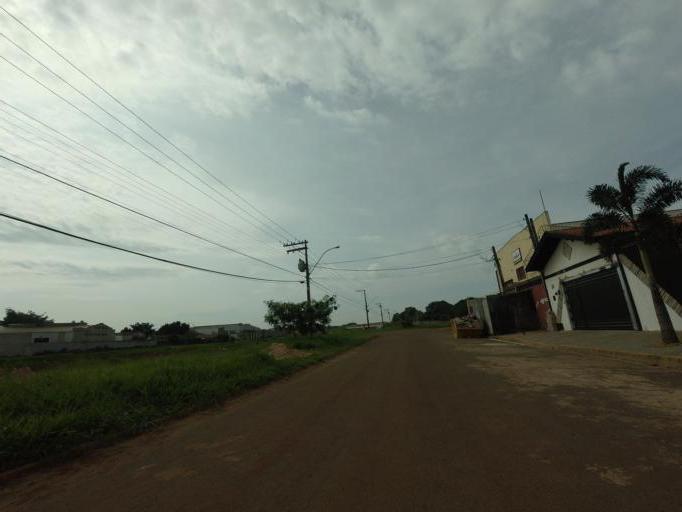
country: BR
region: Sao Paulo
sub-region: Piracicaba
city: Piracicaba
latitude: -22.7618
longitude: -47.5966
